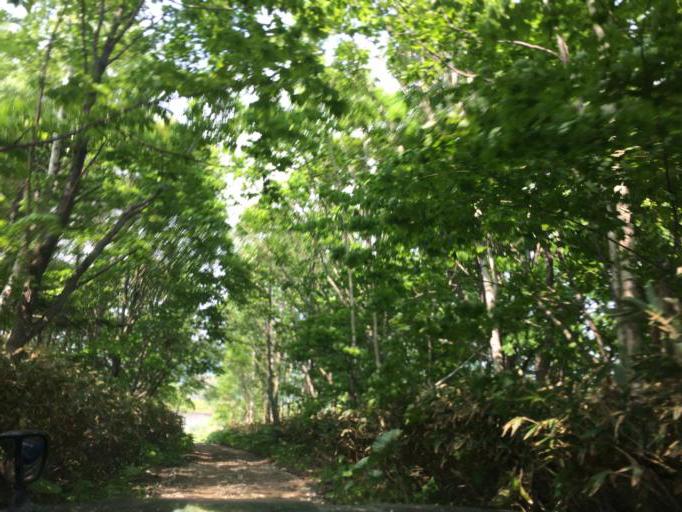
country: JP
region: Hokkaido
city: Niseko Town
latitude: 42.6425
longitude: 140.5010
